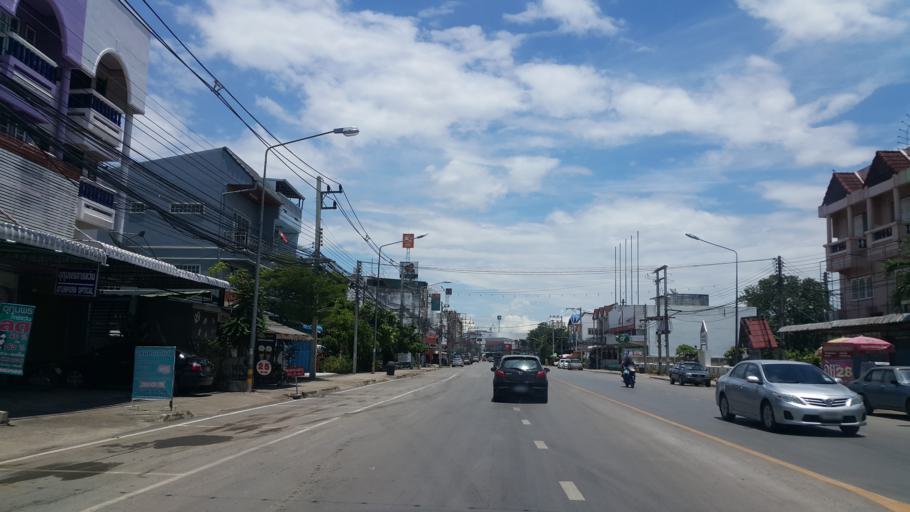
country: TH
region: Phayao
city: Phayao
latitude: 19.1726
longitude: 99.8946
